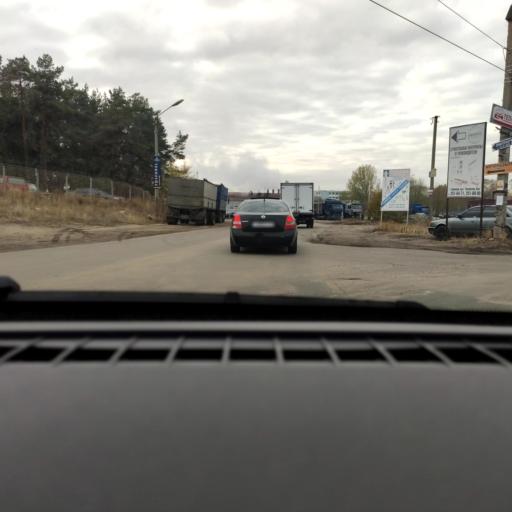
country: RU
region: Voronezj
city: Pridonskoy
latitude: 51.6415
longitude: 39.1113
